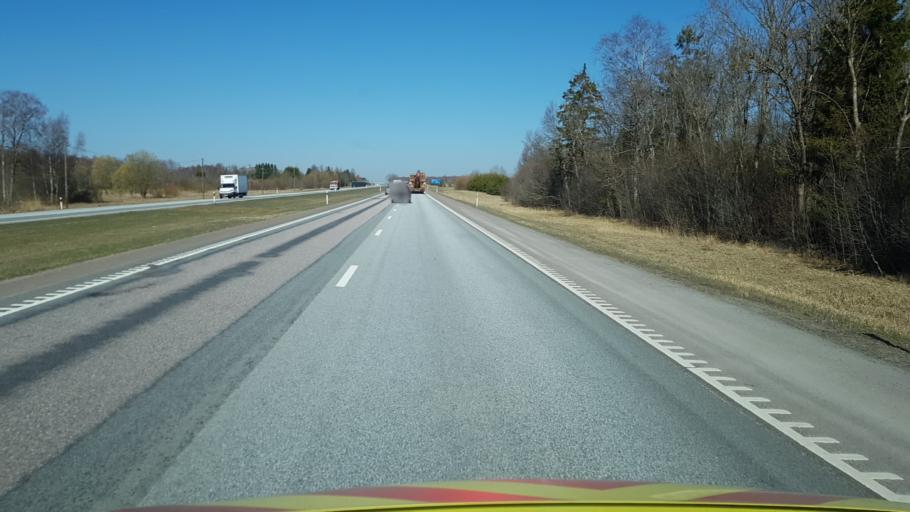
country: EE
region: Harju
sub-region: Rae vald
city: Vaida
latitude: 59.3046
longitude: 24.9444
